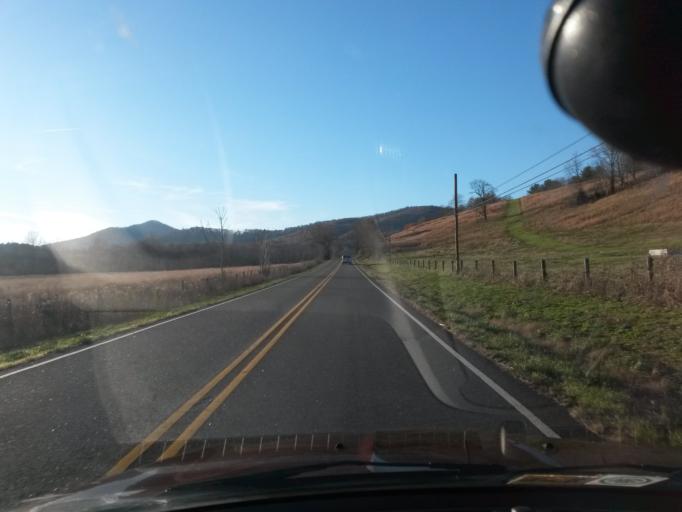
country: US
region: Virginia
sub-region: Amherst County
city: Amherst
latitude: 37.6661
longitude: -79.1993
